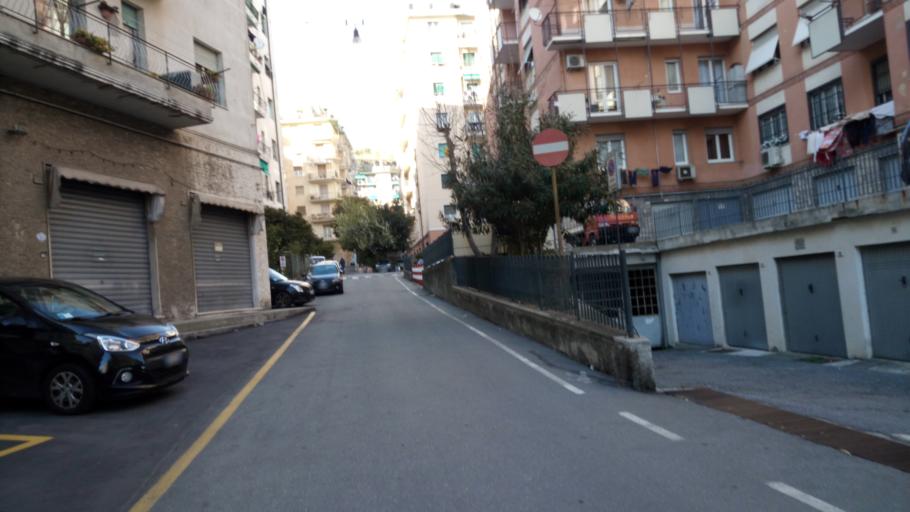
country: IT
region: Liguria
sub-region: Provincia di Genova
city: Mele
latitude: 44.4287
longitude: 8.7727
